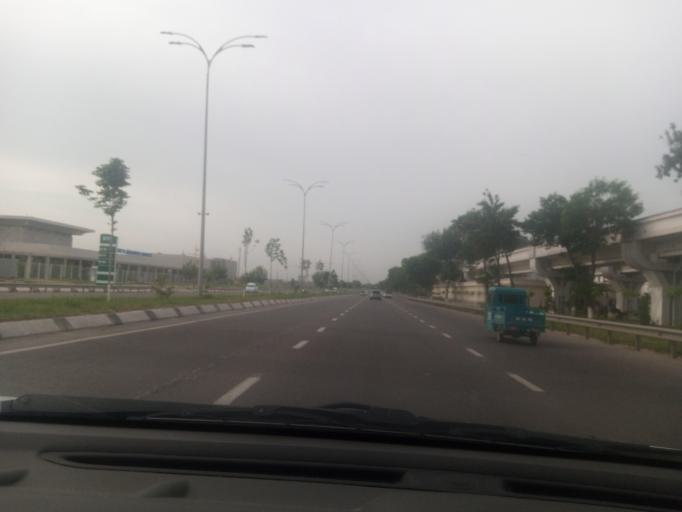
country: UZ
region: Toshkent Shahri
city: Bektemir
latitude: 41.2834
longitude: 69.3605
